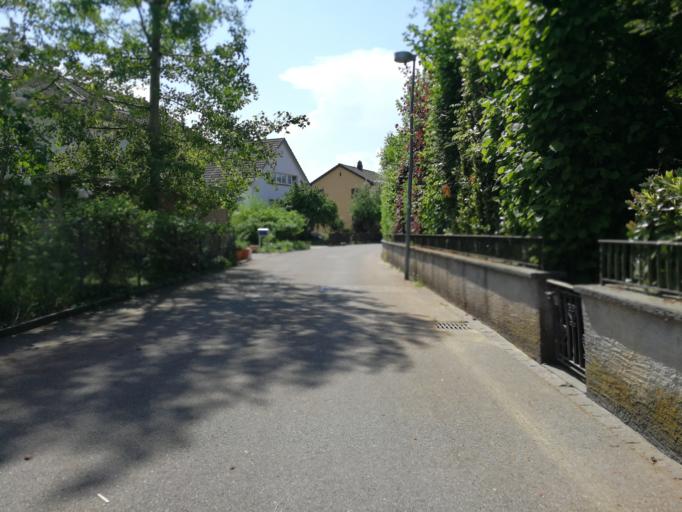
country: CH
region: Saint Gallen
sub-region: Wahlkreis See-Gaster
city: Rapperswil
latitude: 47.2342
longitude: 8.8230
